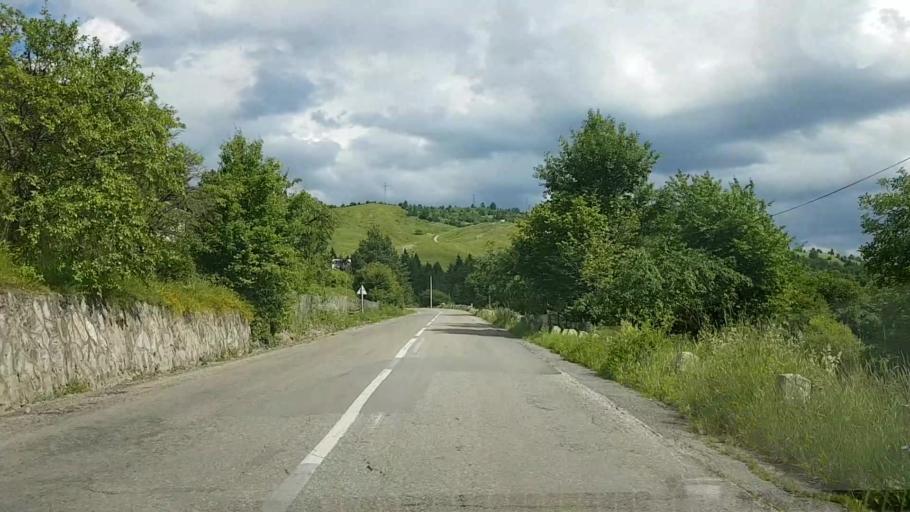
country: RO
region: Neamt
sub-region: Comuna Hangu
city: Hangu
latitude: 47.0069
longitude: 26.0926
